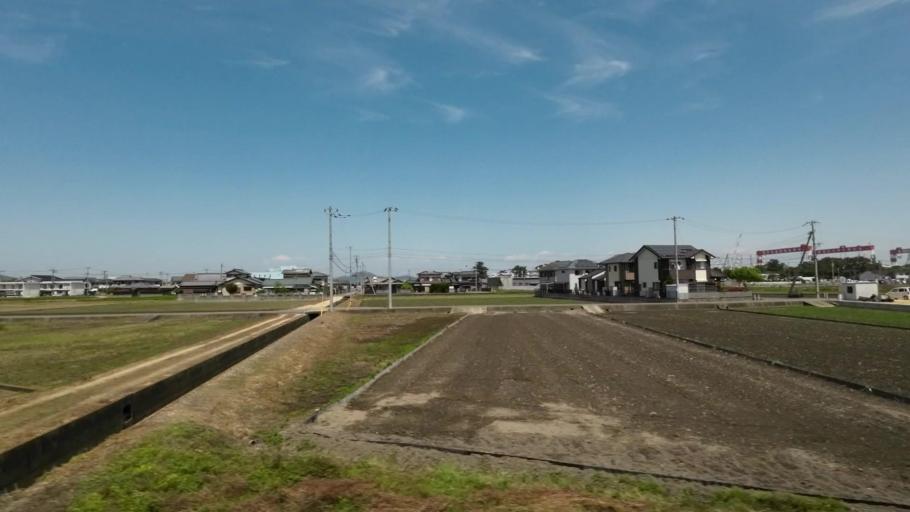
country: JP
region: Kagawa
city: Marugame
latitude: 34.2817
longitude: 133.7680
